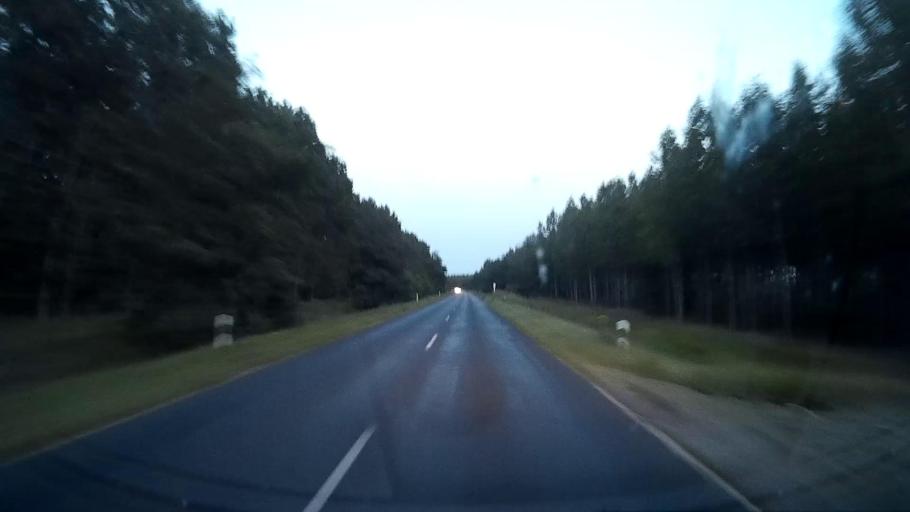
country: HU
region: Pest
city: Cegledbercel
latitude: 47.1982
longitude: 19.7108
